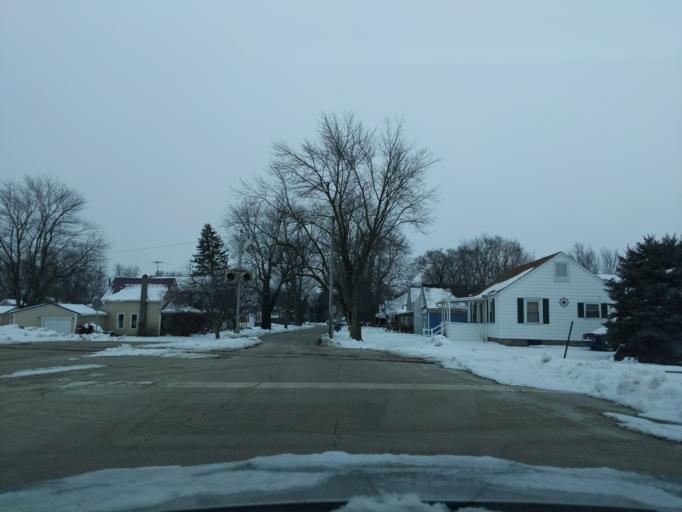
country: US
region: Indiana
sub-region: Benton County
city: Otterbein
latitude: 40.4887
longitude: -87.0962
